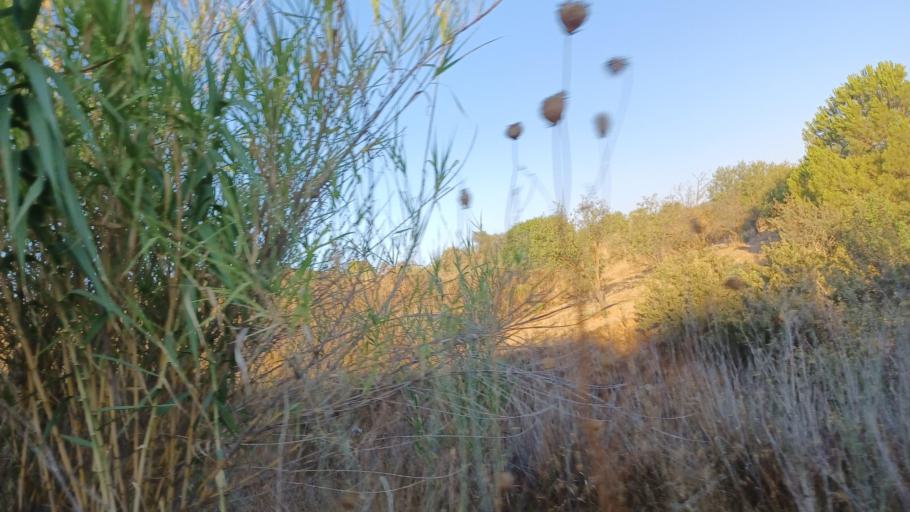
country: CY
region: Pafos
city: Mesogi
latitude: 34.9079
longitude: 32.5244
